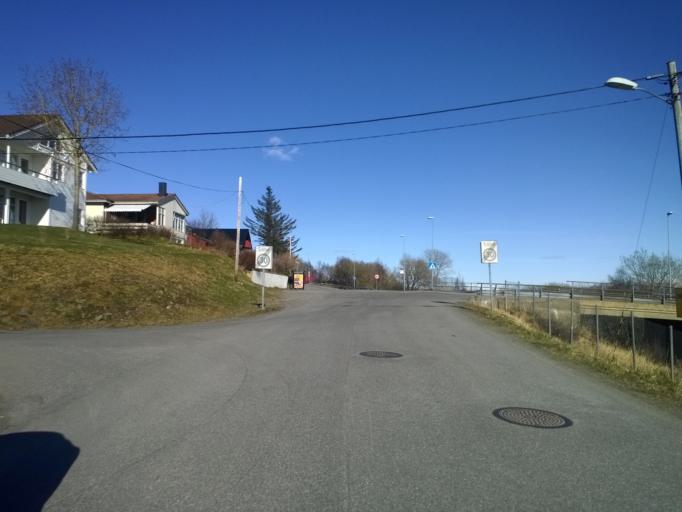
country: NO
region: Nordland
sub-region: Bodo
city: Lopsmarka
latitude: 67.2783
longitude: 14.5089
